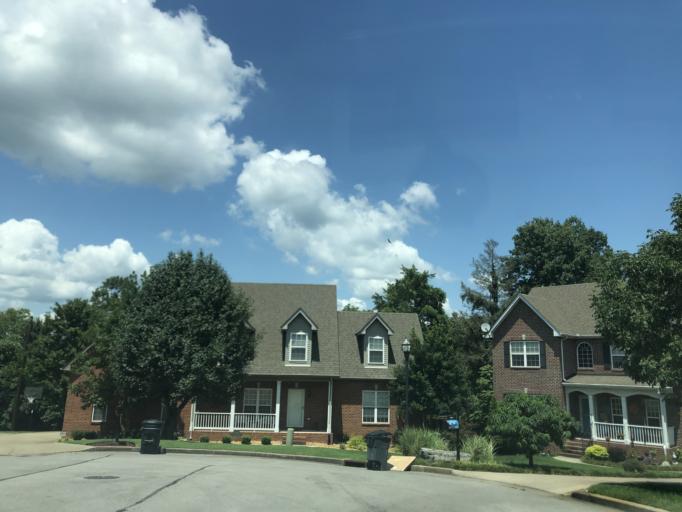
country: US
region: Tennessee
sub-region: Wilson County
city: Green Hill
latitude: 36.1990
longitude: -86.5908
